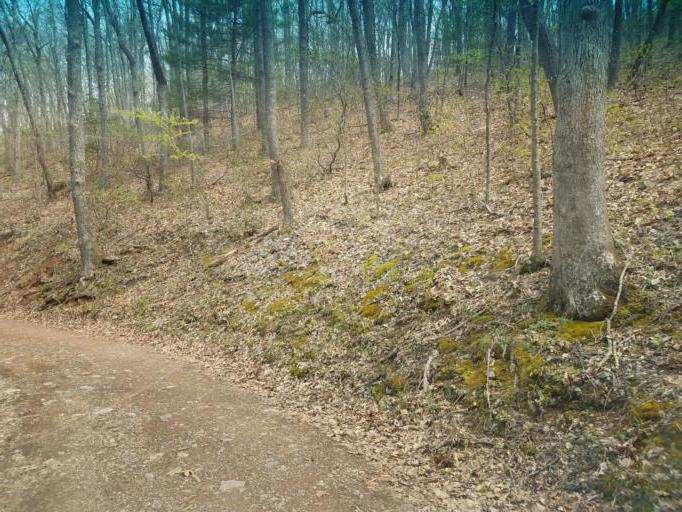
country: US
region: Virginia
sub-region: Smyth County
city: Marion
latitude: 36.7885
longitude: -81.4705
